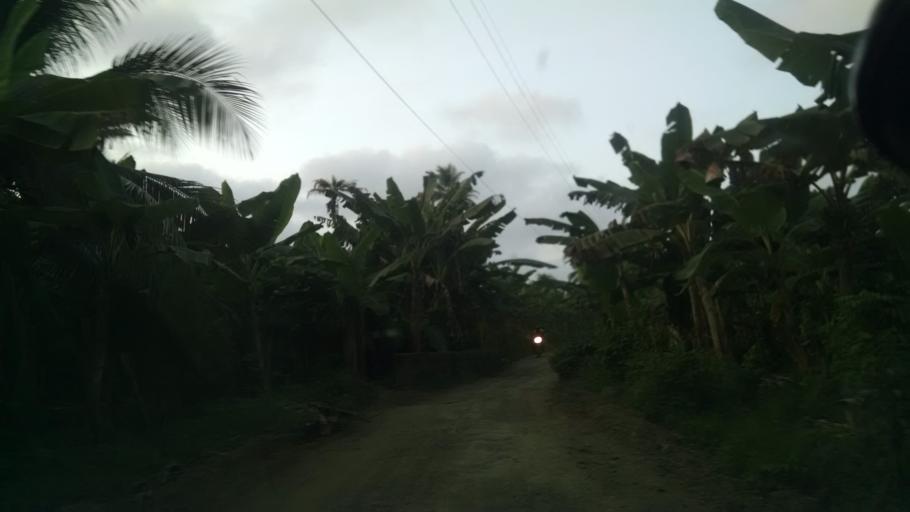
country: CO
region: Antioquia
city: San Juan de Uraba
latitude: 8.7314
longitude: -76.6056
